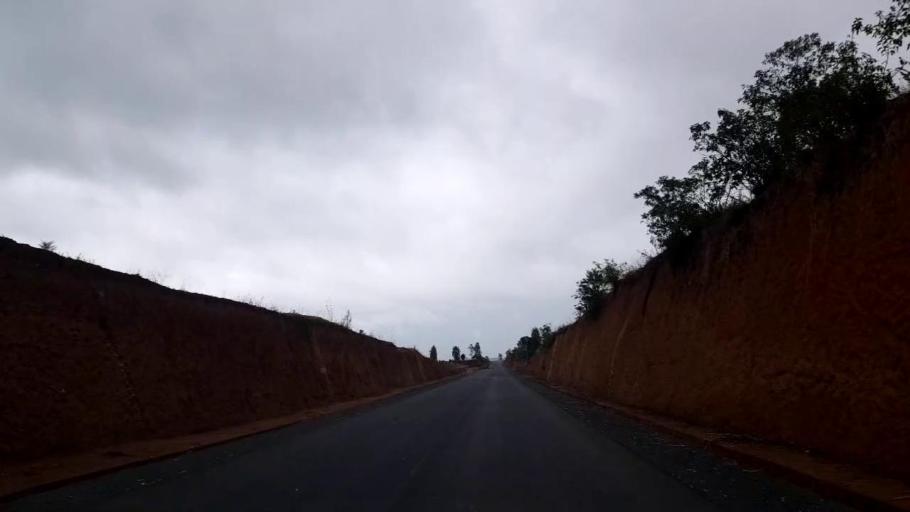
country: RW
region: Northern Province
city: Byumba
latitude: -1.4301
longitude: 30.2635
